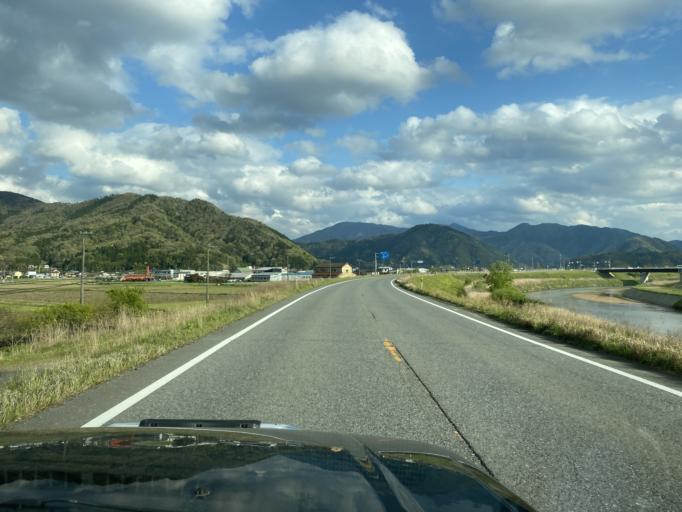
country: JP
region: Hyogo
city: Toyooka
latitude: 35.4840
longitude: 134.8607
